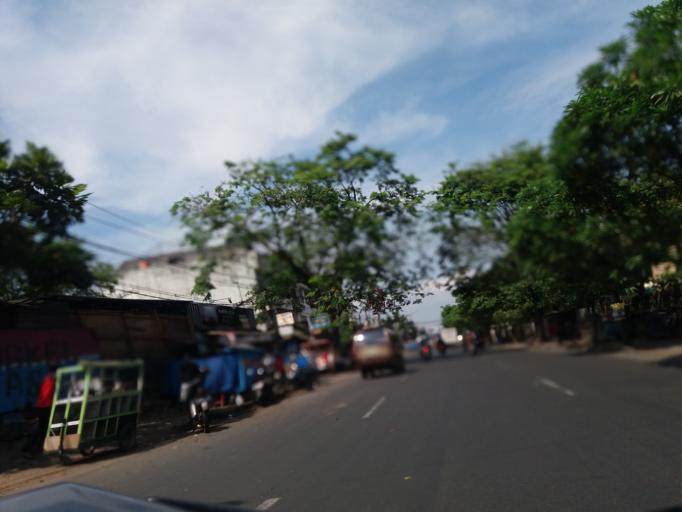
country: ID
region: West Java
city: Bandung
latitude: -6.9102
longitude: 107.6433
